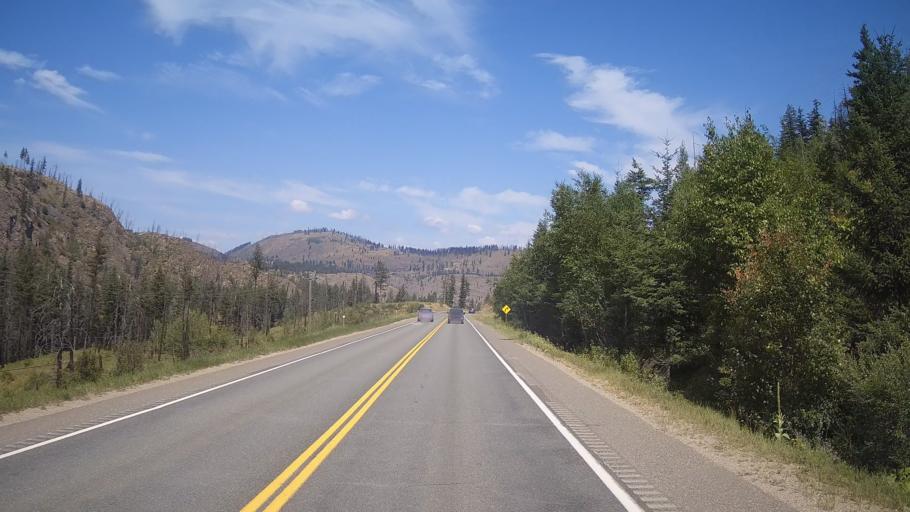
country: CA
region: British Columbia
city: Kamloops
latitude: 51.0838
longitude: -120.1846
